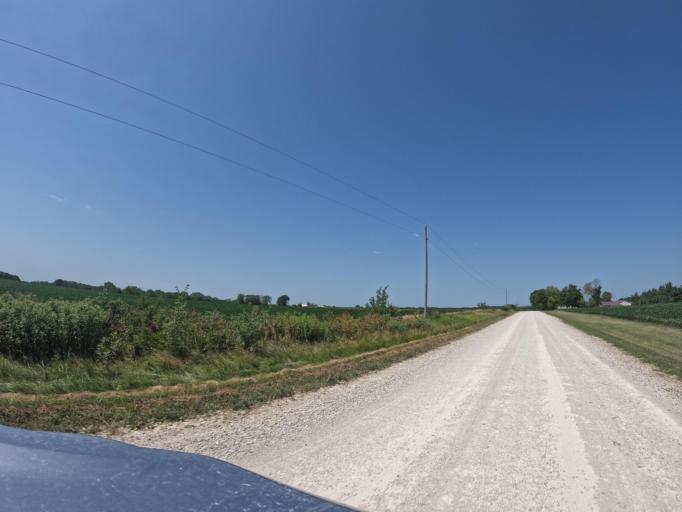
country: US
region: Iowa
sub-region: Henry County
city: Mount Pleasant
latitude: 40.8893
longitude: -91.5890
